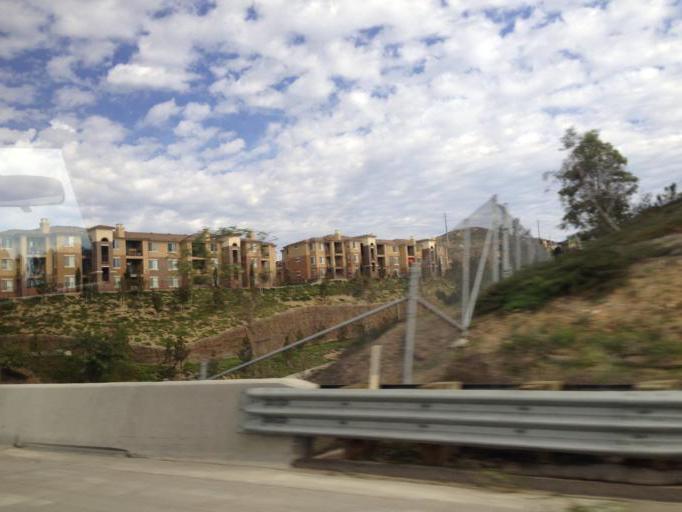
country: US
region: California
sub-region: San Diego County
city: Imperial Beach
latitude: 32.5733
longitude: -117.0391
